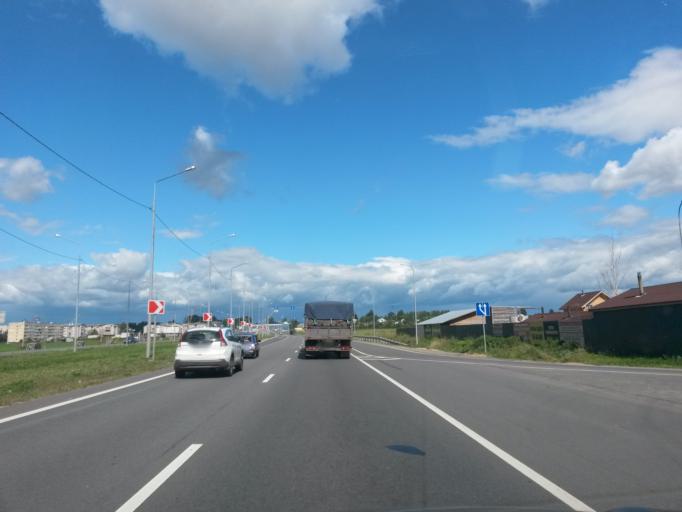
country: RU
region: Jaroslavl
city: Yaroslavl
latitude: 57.6960
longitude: 39.8992
